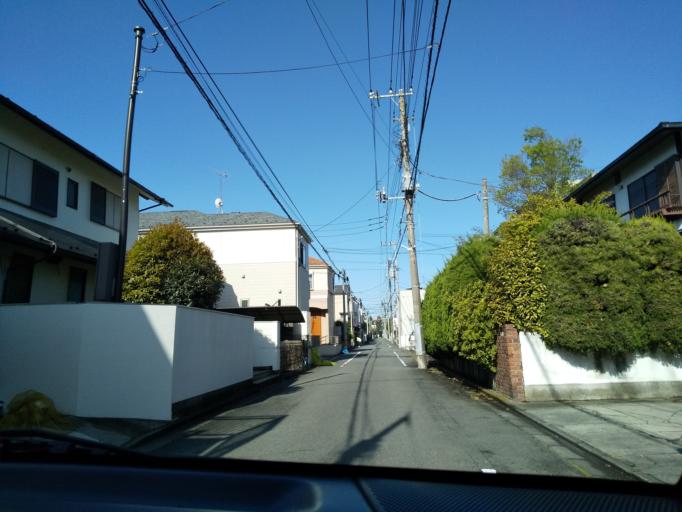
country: JP
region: Tokyo
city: Kokubunji
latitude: 35.6925
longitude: 139.4380
